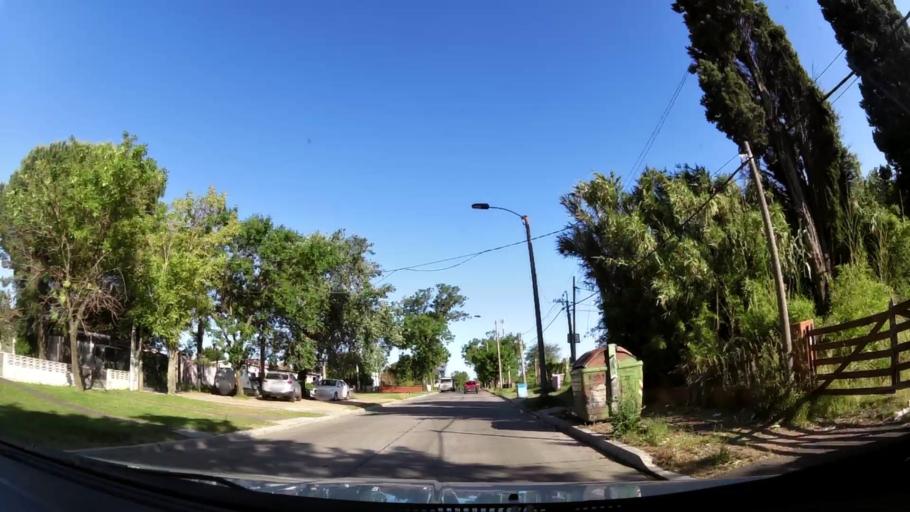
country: UY
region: Canelones
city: La Paz
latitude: -34.8183
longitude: -56.2159
